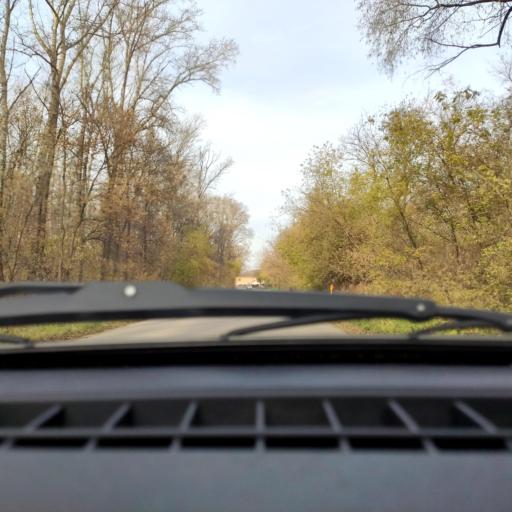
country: RU
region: Bashkortostan
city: Ufa
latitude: 54.7945
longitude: 56.1545
